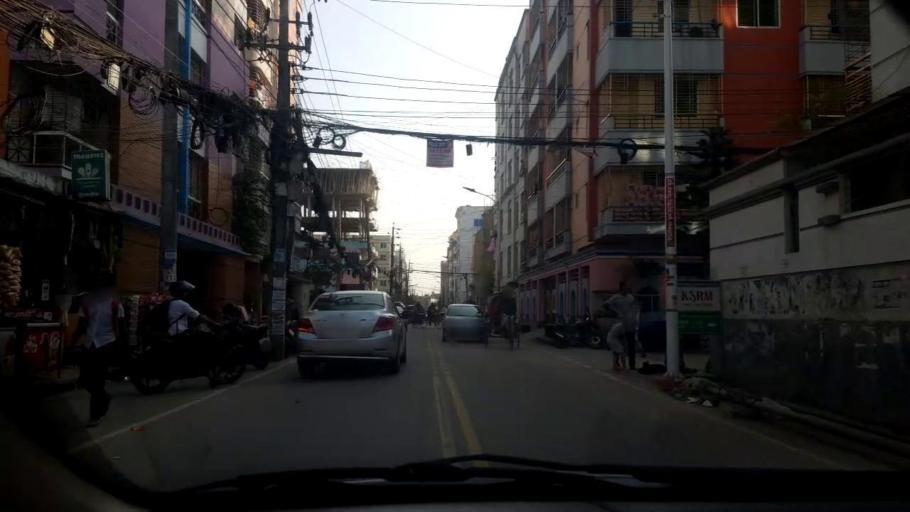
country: BD
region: Dhaka
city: Tungi
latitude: 23.8697
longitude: 90.3834
